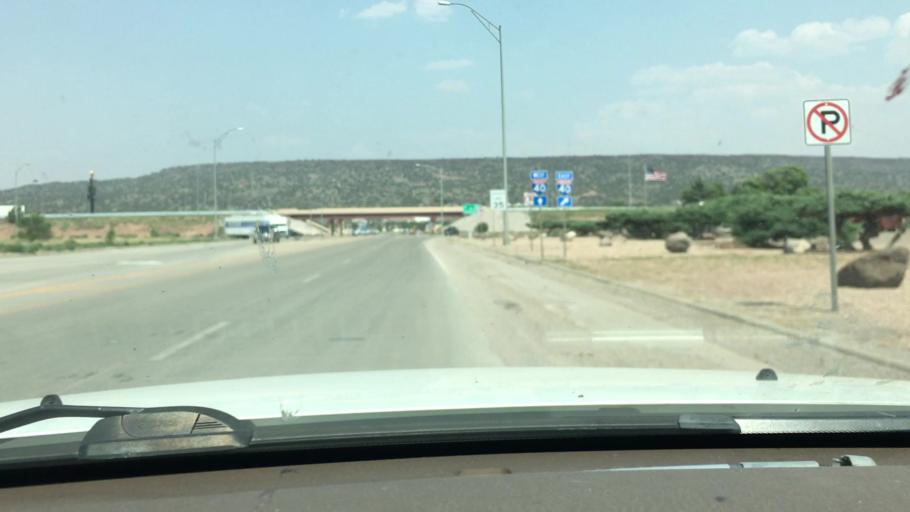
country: US
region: New Mexico
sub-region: Cibola County
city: Milan
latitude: 35.1819
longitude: -107.9045
